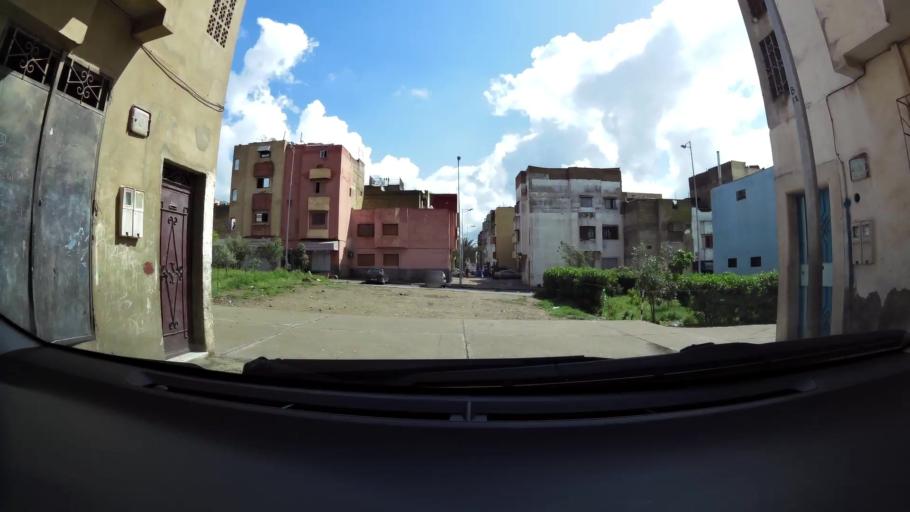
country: MA
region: Grand Casablanca
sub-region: Mediouna
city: Tit Mellil
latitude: 33.5477
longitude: -7.4874
